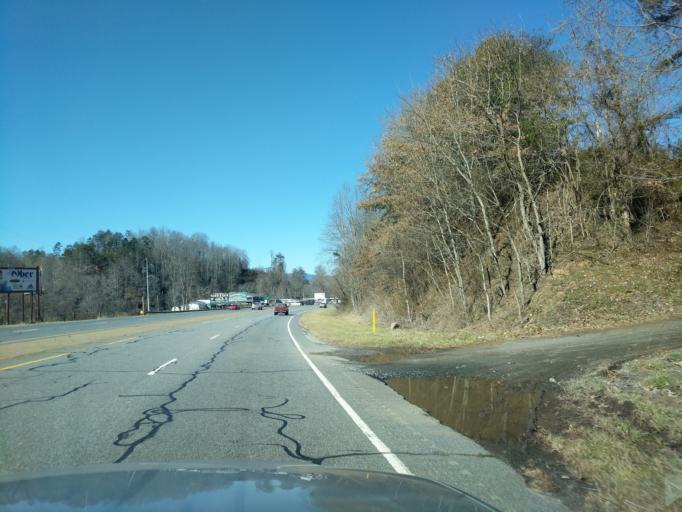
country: US
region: North Carolina
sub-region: Swain County
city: Cherokee
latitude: 35.4070
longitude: -83.3244
